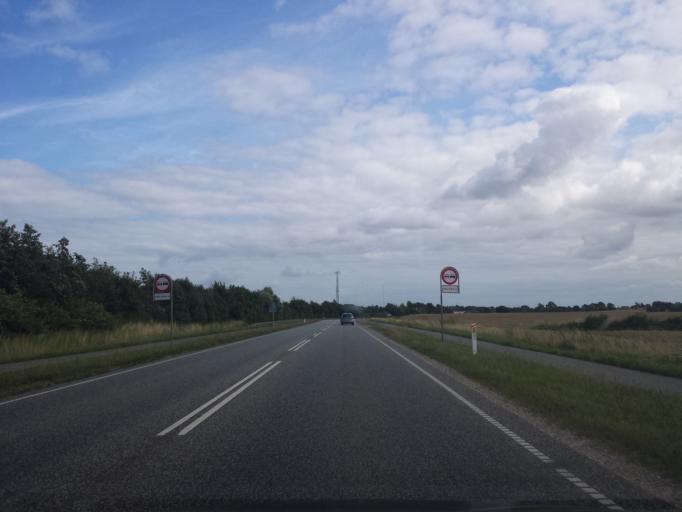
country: DK
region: South Denmark
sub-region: Sonderborg Kommune
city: Guderup
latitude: 54.9975
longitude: 9.8524
